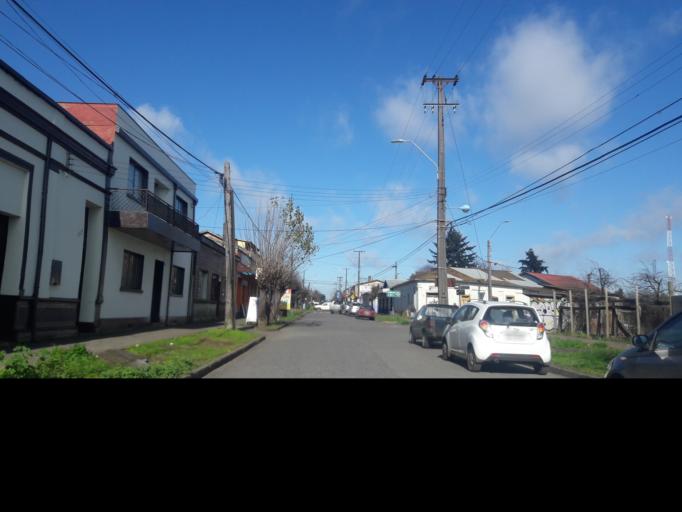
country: CL
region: Araucania
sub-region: Provincia de Malleco
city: Victoria
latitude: -38.2357
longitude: -72.3295
